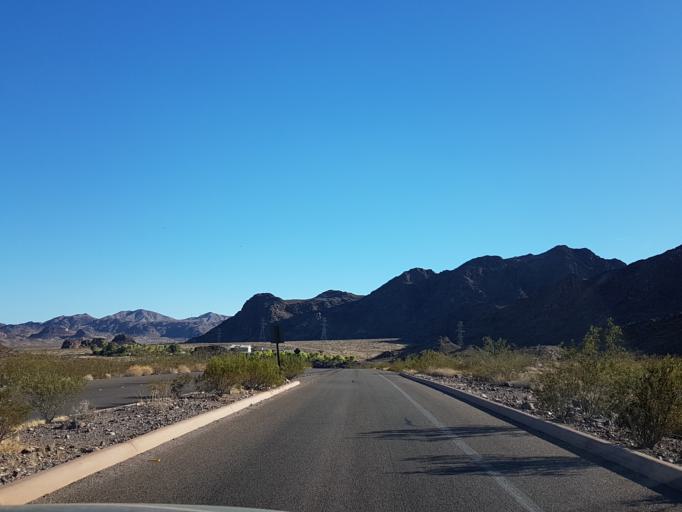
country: US
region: Nevada
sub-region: Clark County
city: Boulder City
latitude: 36.0528
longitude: -114.8196
